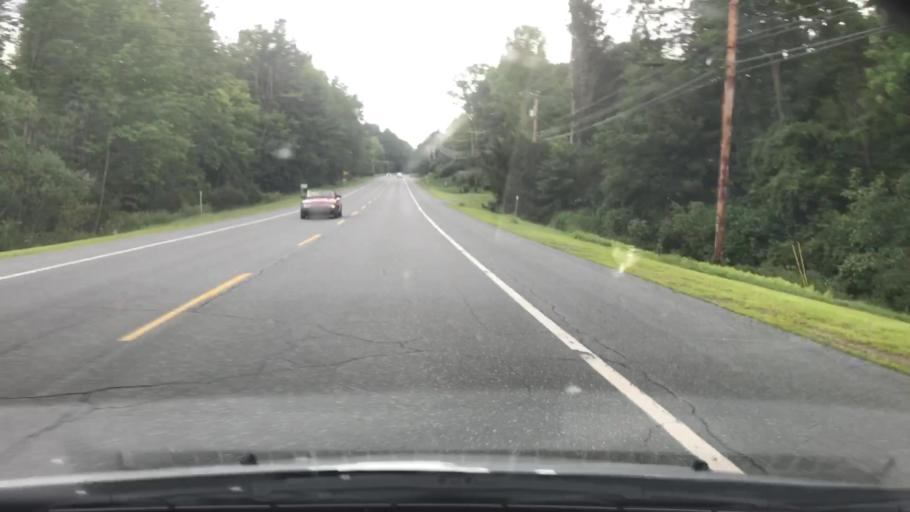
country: US
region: New Hampshire
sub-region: Grafton County
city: Lyme
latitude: 43.7769
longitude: -72.1818
